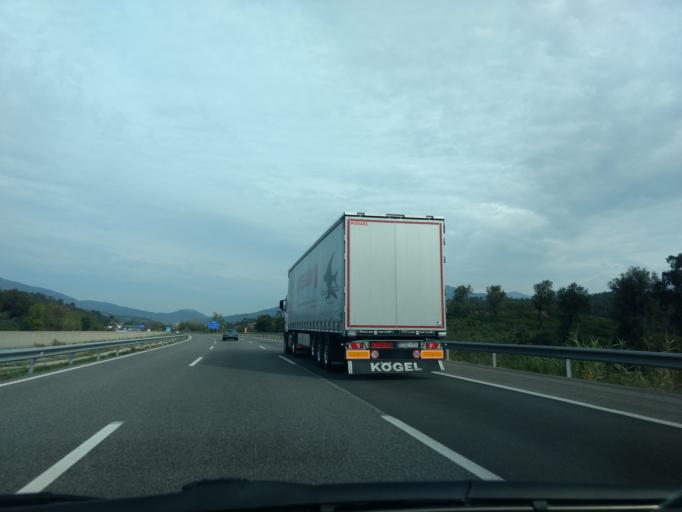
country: ES
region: Catalonia
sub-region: Provincia de Girona
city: Capmany
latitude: 42.3815
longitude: 2.8859
